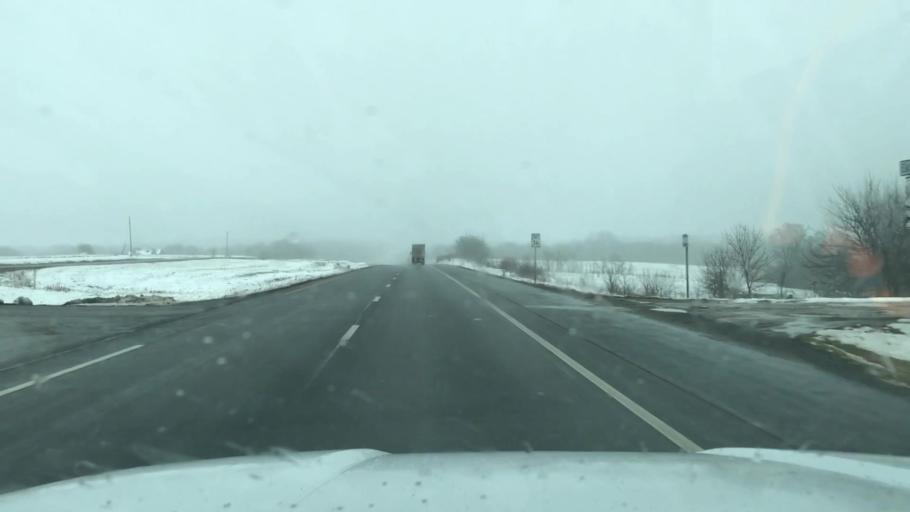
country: US
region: Missouri
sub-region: DeKalb County
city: Maysville
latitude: 39.7620
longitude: -94.4940
